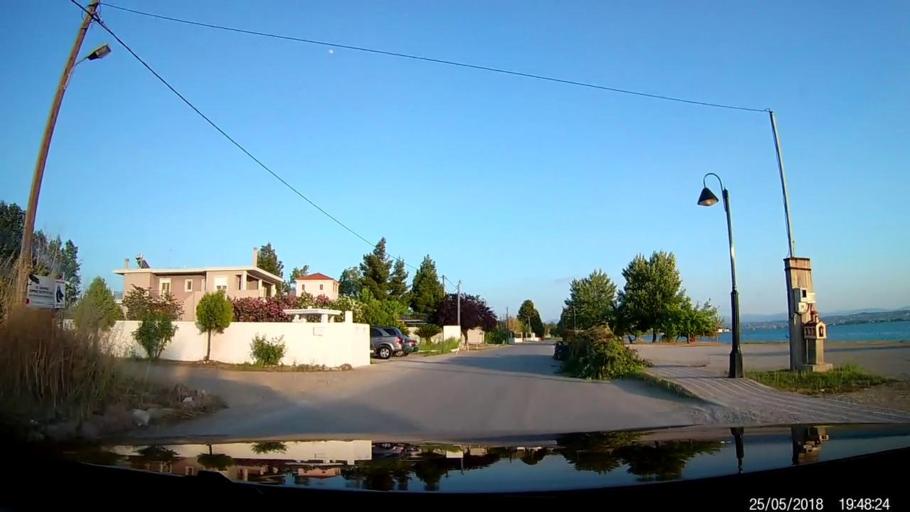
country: GR
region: Central Greece
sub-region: Nomos Evvoias
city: Ayios Nikolaos
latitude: 38.4175
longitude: 23.6388
